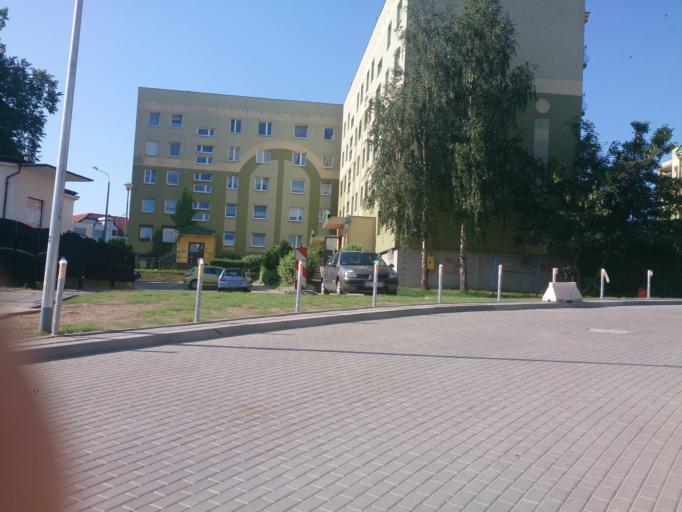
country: PL
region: Pomeranian Voivodeship
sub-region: Gdynia
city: Wielki Kack
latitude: 54.4692
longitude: 18.4881
